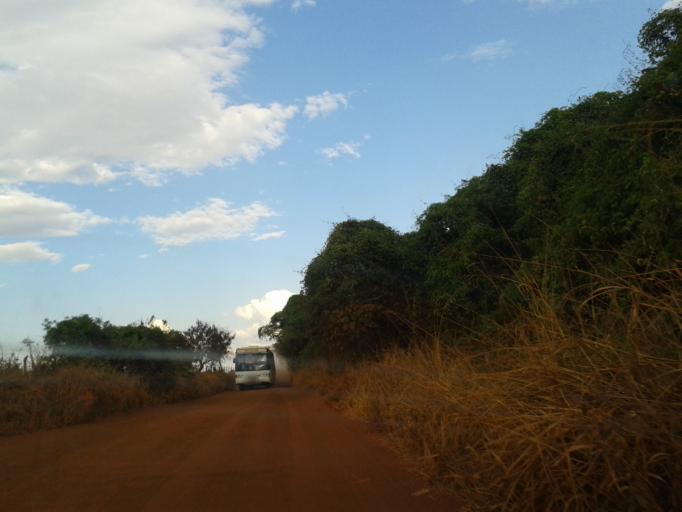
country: BR
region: Minas Gerais
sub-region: Ituiutaba
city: Ituiutaba
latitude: -19.2014
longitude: -49.8148
